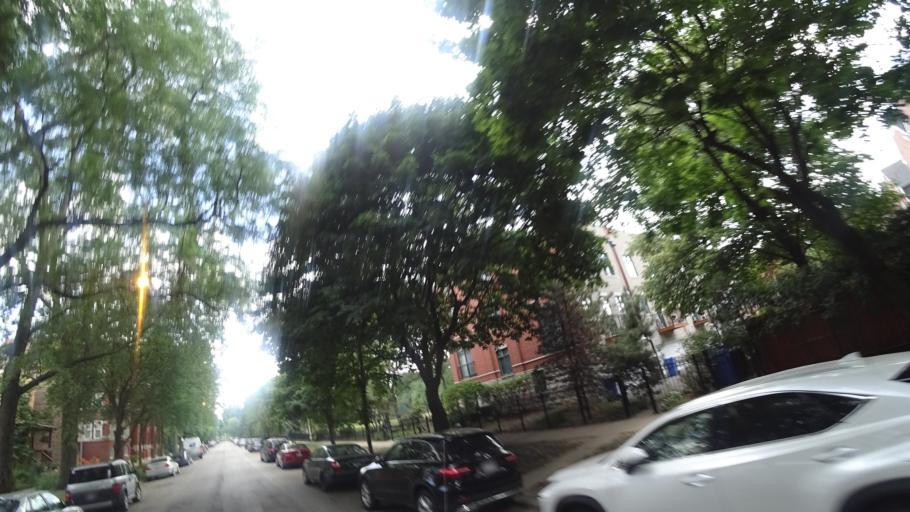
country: US
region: Illinois
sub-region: Cook County
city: Chicago
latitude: 41.7977
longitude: -87.5997
